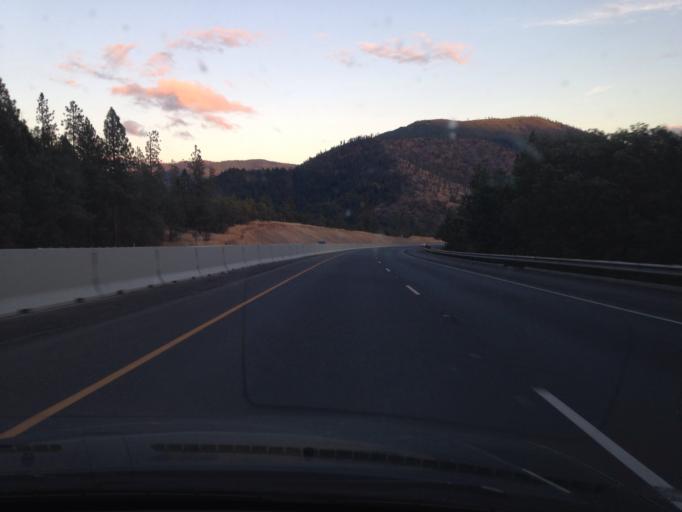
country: US
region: Oregon
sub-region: Josephine County
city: Merlin
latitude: 42.5799
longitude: -123.3774
